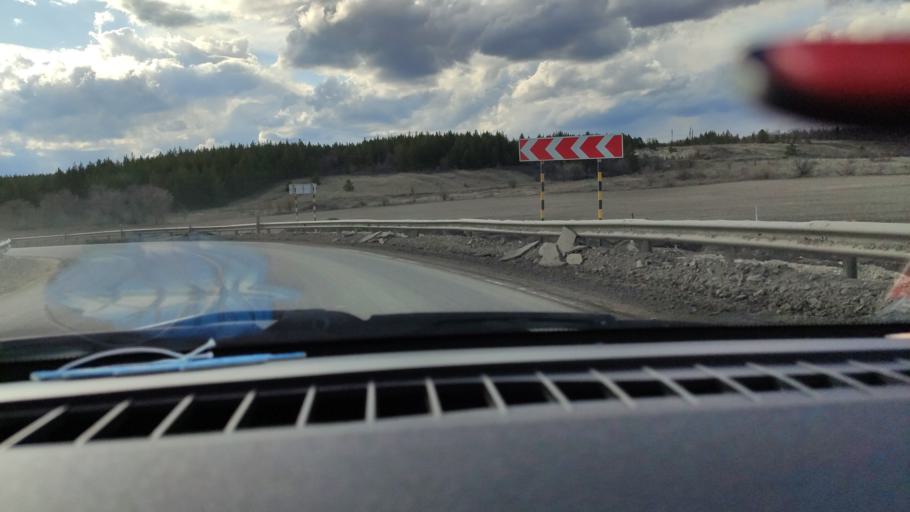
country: RU
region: Saratov
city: Sinodskoye
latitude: 52.0126
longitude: 46.6896
